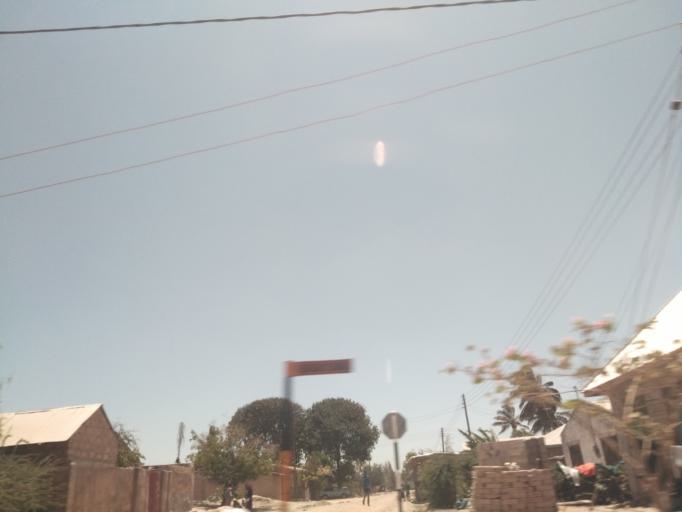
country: TZ
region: Dodoma
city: Dodoma
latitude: -6.1579
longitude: 35.7387
